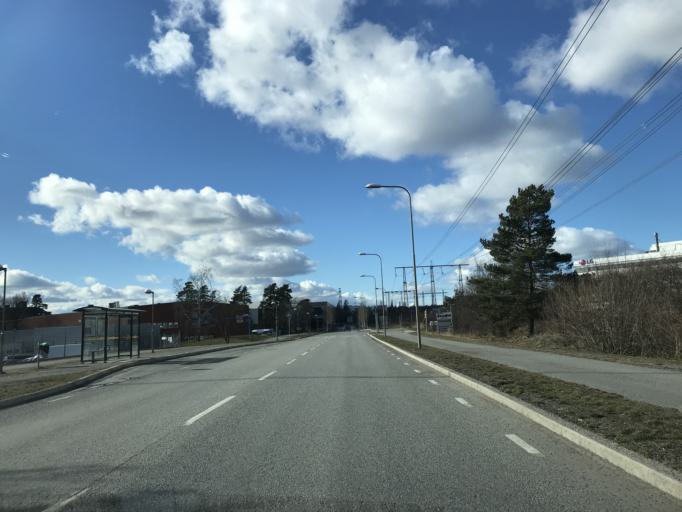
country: SE
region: Stockholm
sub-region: Stockholms Kommun
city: Kista
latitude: 59.4186
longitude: 17.9272
